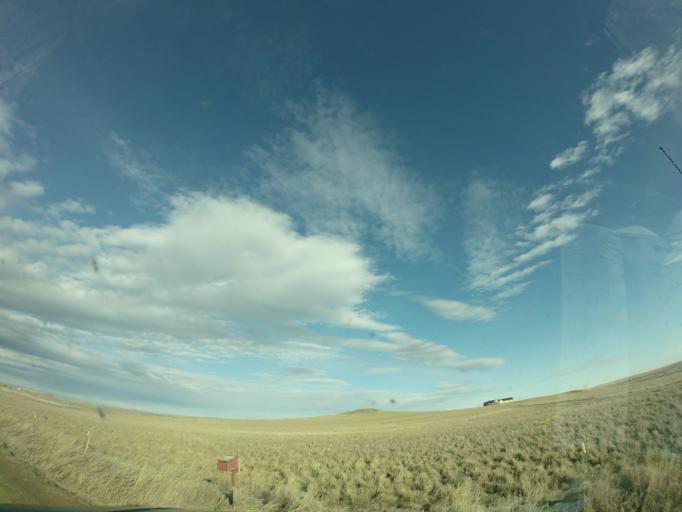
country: US
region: Montana
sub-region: Yellowstone County
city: Laurel
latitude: 45.8621
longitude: -108.8814
